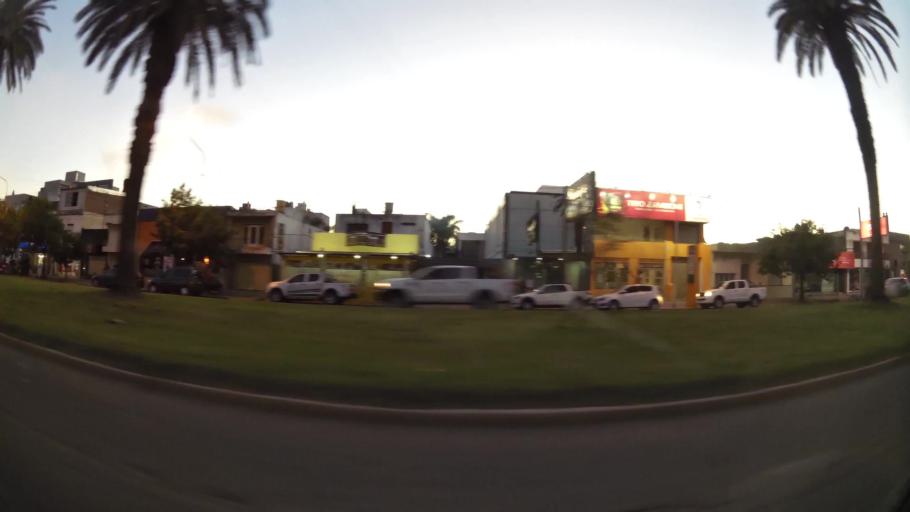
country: AR
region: Cordoba
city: Villa Maria
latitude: -32.4059
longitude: -63.2411
